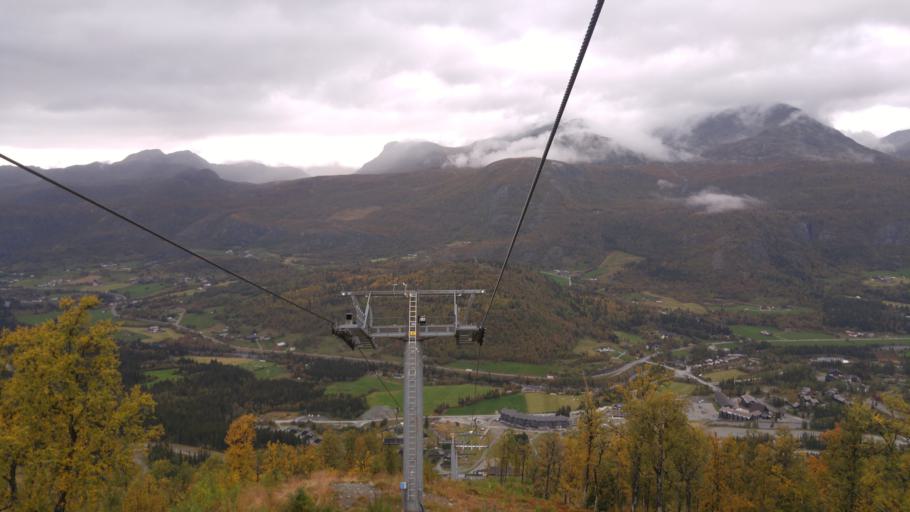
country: NO
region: Buskerud
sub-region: Hemsedal
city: Hemsedal
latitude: 60.8538
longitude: 8.5123
